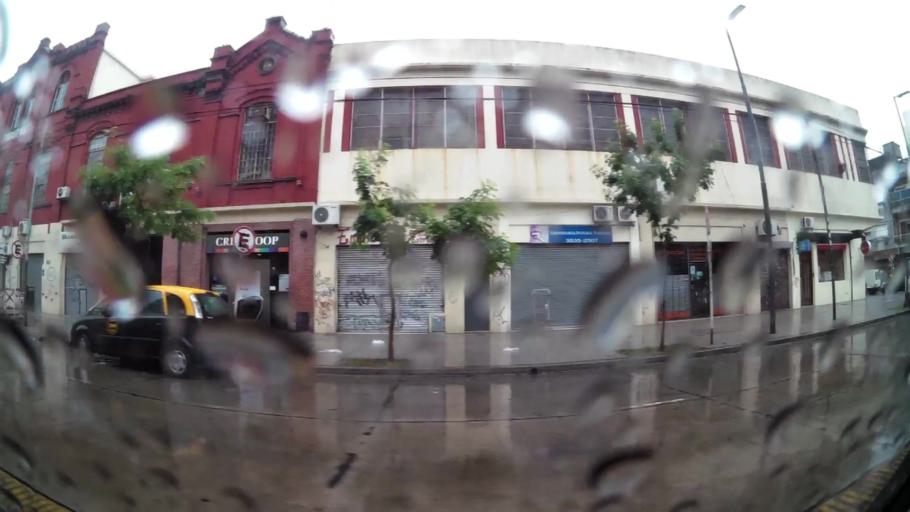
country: AR
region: Buenos Aires F.D.
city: Buenos Aires
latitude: -34.6349
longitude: -58.3701
